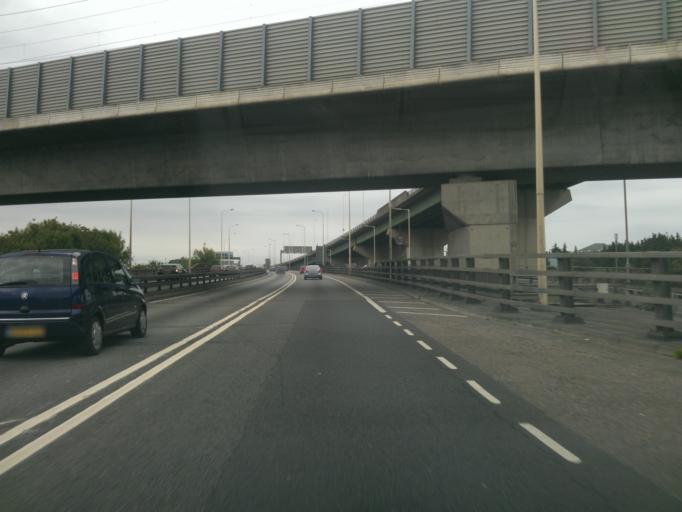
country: GB
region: England
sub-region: Kent
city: West Thurrock
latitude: 51.4736
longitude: 0.2653
